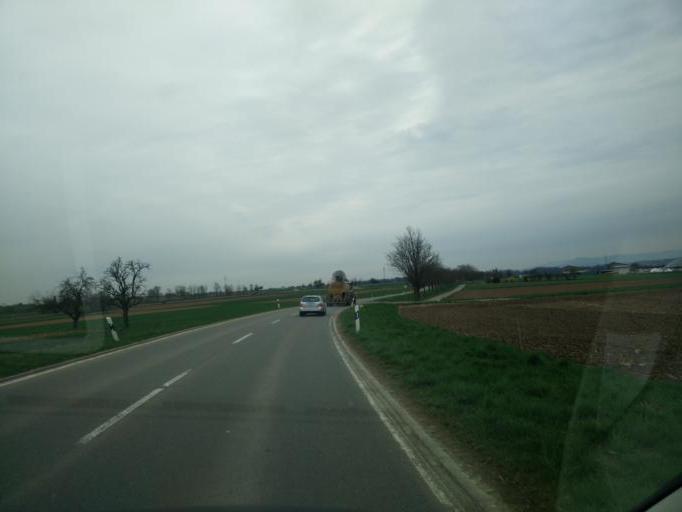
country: DE
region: Baden-Wuerttemberg
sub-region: Tuebingen Region
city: Kusterdingen
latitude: 48.5037
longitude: 9.1022
